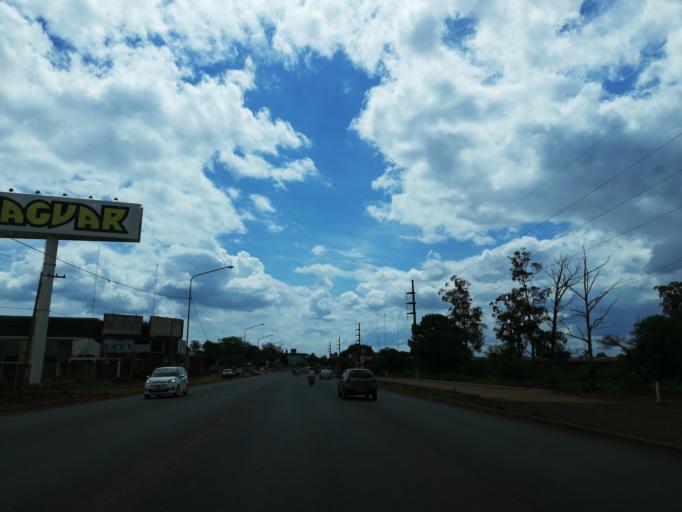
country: AR
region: Misiones
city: Garupa
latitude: -27.4395
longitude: -55.8800
